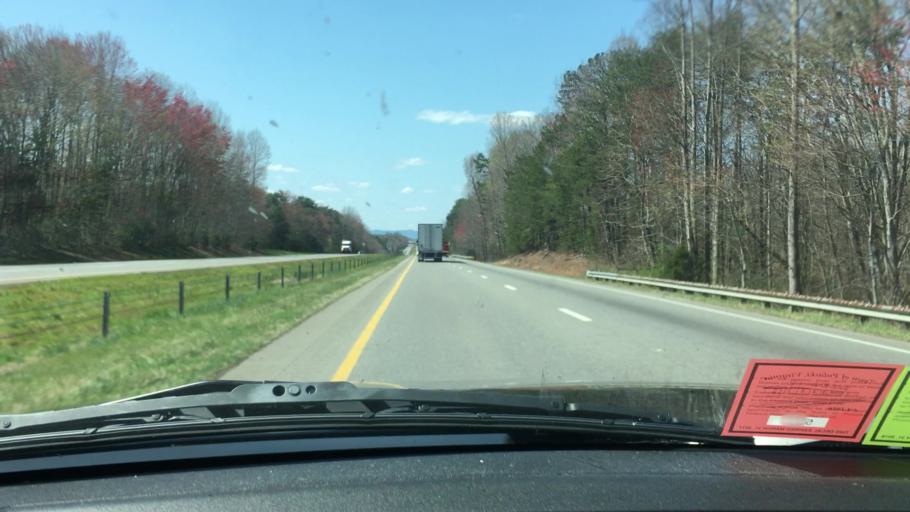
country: US
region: North Carolina
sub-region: Surry County
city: Pilot Mountain
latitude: 36.4195
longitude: -80.5127
